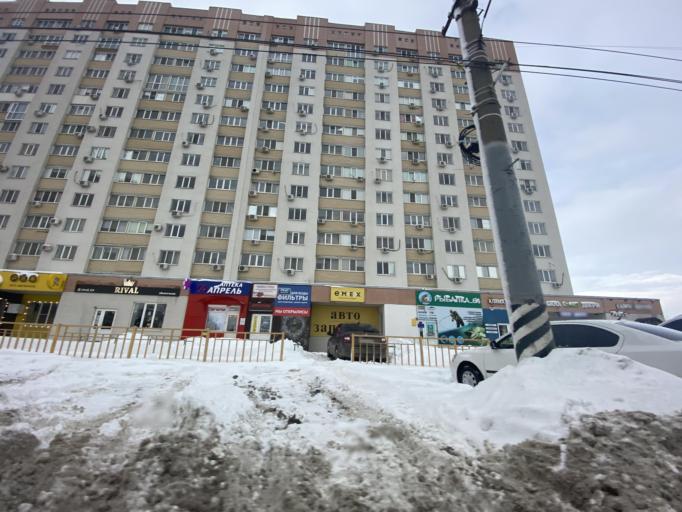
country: RU
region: Saratov
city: Engel's
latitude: 51.4994
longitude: 46.0975
